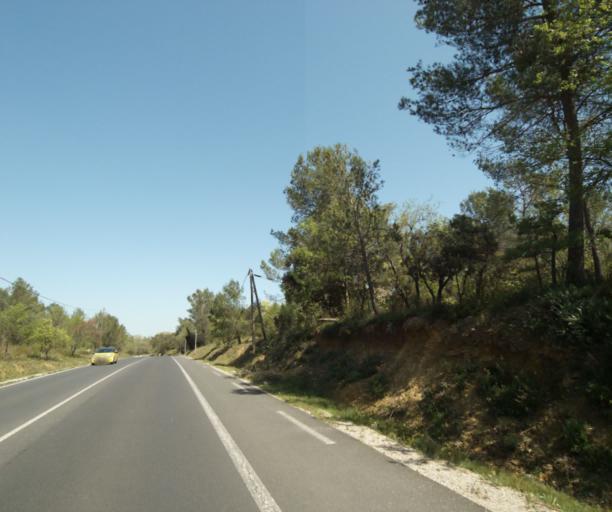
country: FR
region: Languedoc-Roussillon
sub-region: Departement de l'Herault
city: Montferrier-sur-Lez
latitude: 43.6626
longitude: 3.8664
